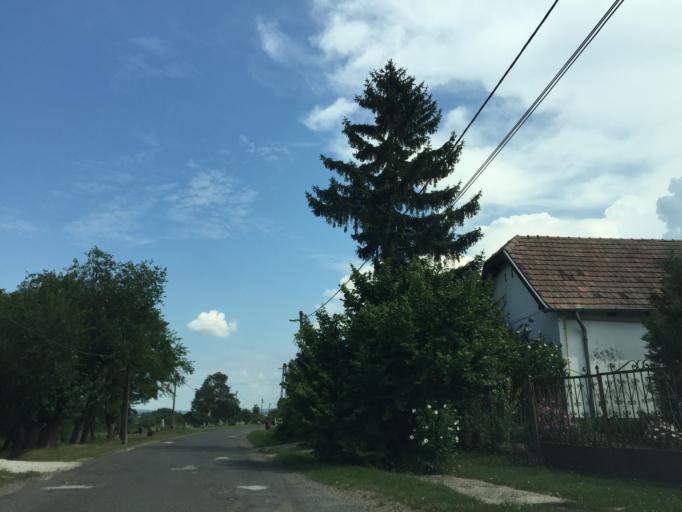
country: HU
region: Nograd
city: Nagyoroszi
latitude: 47.9749
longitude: 19.1043
